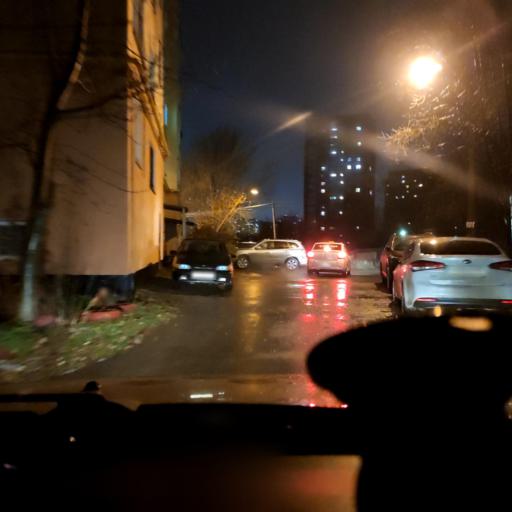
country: RU
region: Perm
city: Perm
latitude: 57.9617
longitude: 56.2138
